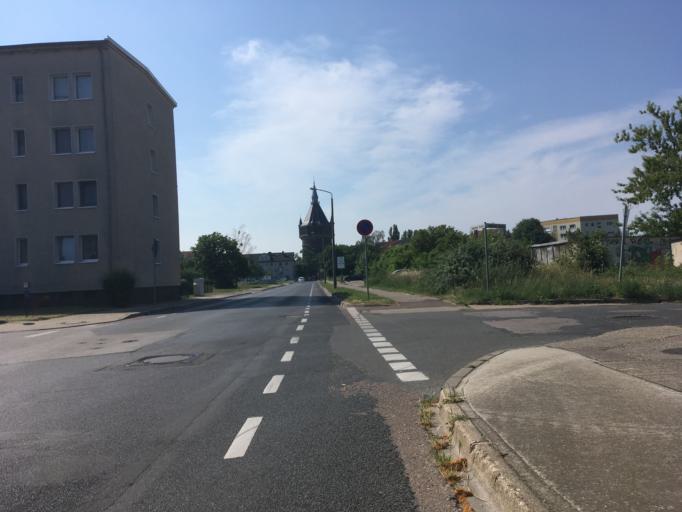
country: DE
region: Saxony-Anhalt
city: Dessau
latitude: 51.8237
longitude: 12.2352
